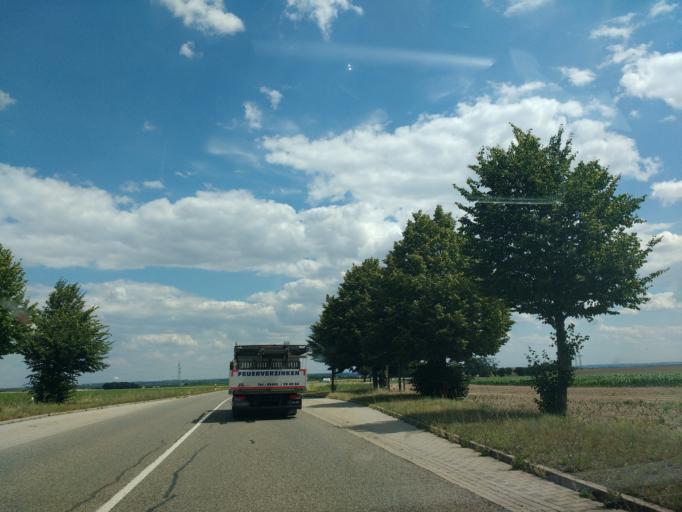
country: DE
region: Saxony-Anhalt
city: Droyssig
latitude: 51.0739
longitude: 12.0085
